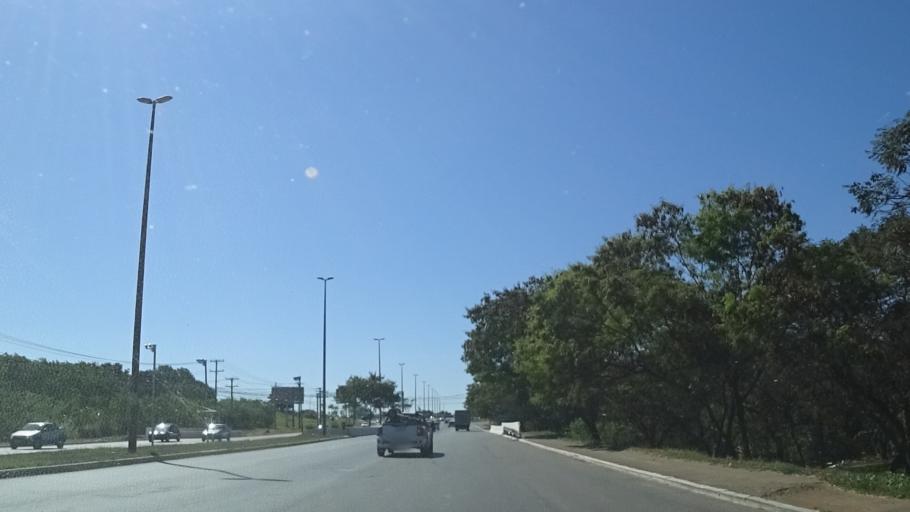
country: BR
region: Federal District
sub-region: Brasilia
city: Brasilia
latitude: -15.8643
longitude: -47.9609
